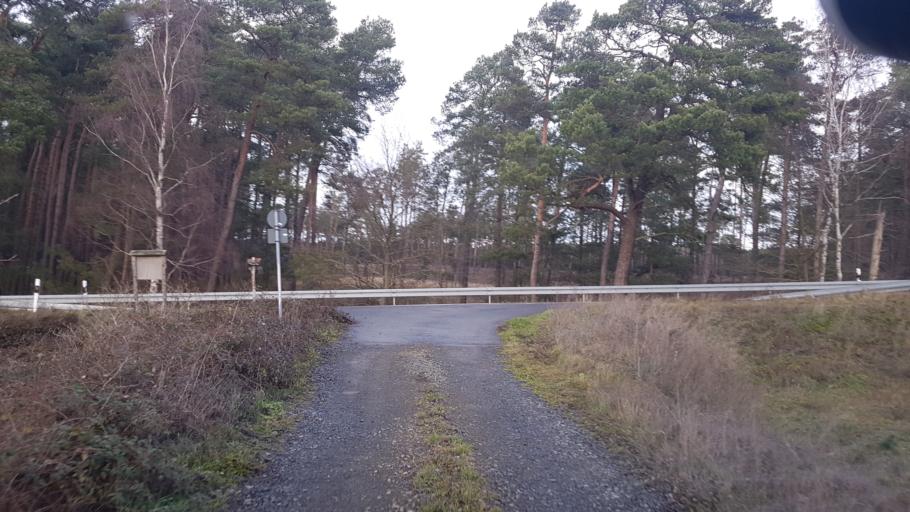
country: DE
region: Brandenburg
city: Hohenbucko
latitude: 51.7390
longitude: 13.4794
